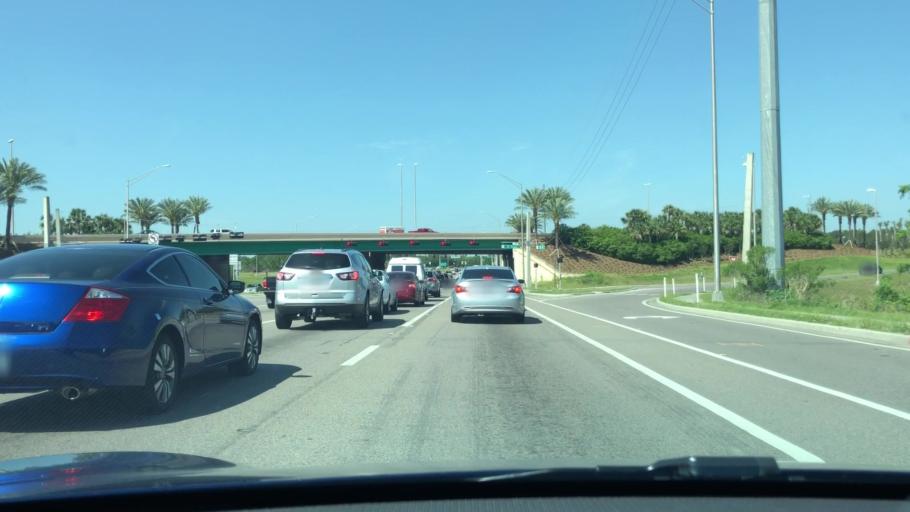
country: US
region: Florida
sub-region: Orange County
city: Oakland
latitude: 28.5489
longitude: -81.6416
